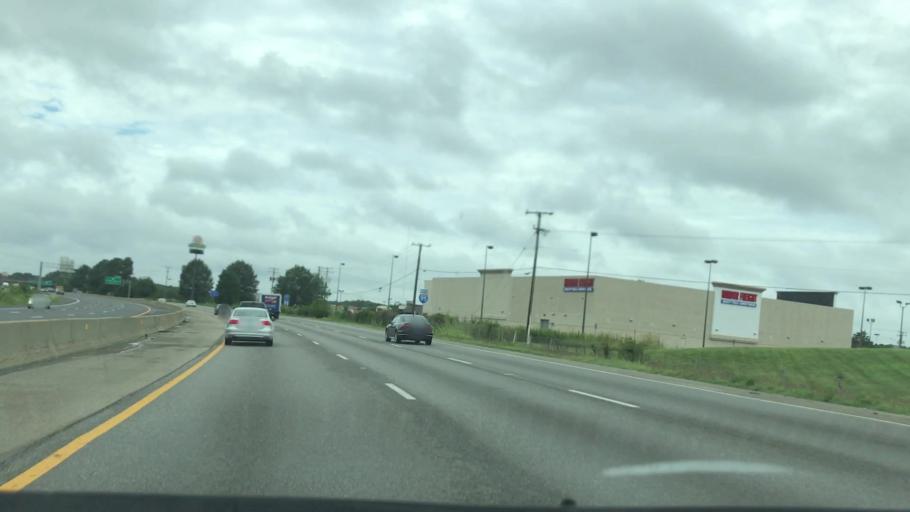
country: US
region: Virginia
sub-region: City of Petersburg
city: Petersburg
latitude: 37.2484
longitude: -77.3932
